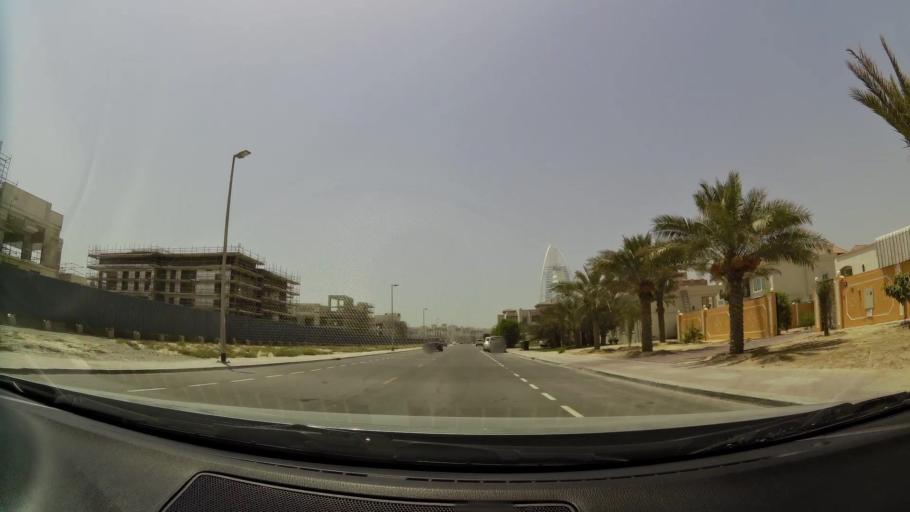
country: AE
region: Dubai
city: Dubai
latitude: 25.1331
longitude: 55.1931
